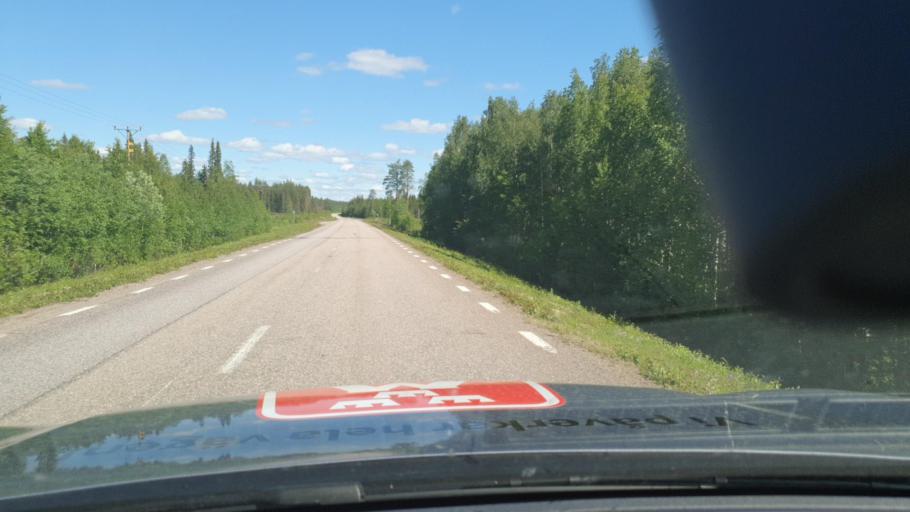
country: SE
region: Norrbotten
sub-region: Overkalix Kommun
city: OEverkalix
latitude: 67.0587
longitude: 22.5117
